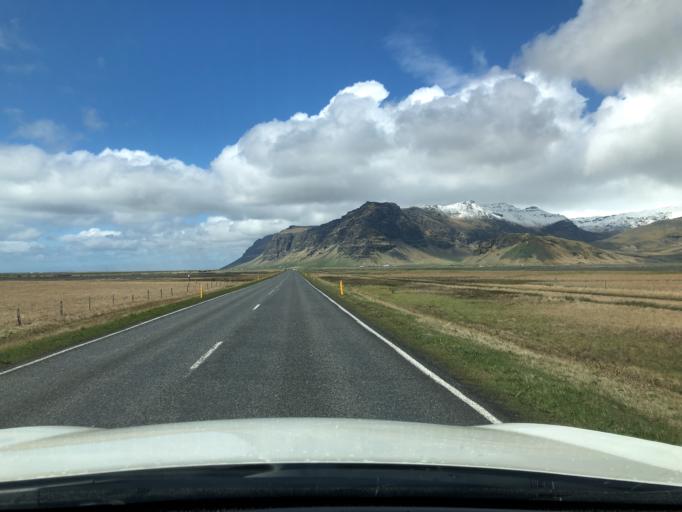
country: IS
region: South
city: Vestmannaeyjar
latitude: 63.5264
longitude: -19.5944
